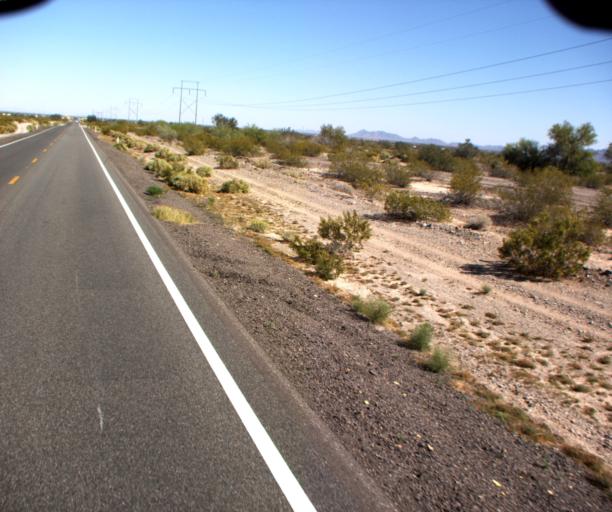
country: US
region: Arizona
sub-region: La Paz County
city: Quartzsite
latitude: 33.6399
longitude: -114.2171
